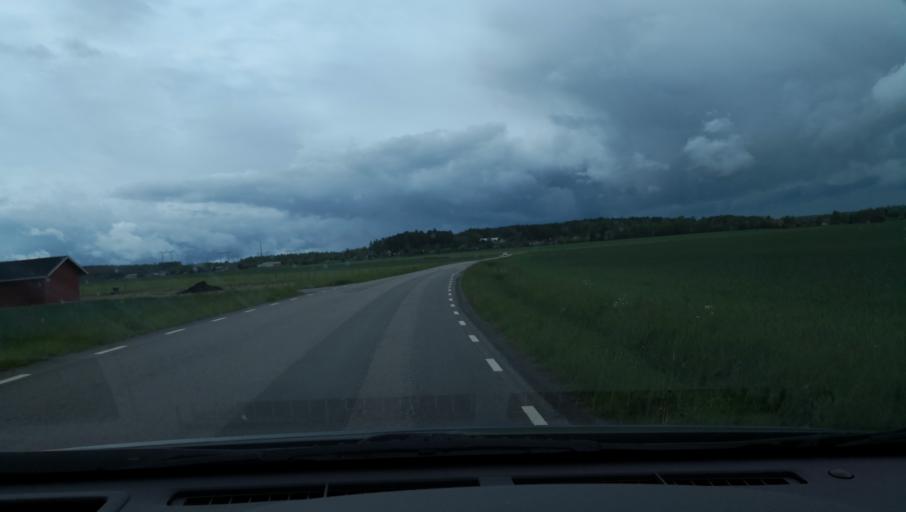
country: SE
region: Uppsala
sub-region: Enkopings Kommun
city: Orsundsbro
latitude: 59.7244
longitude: 17.3156
